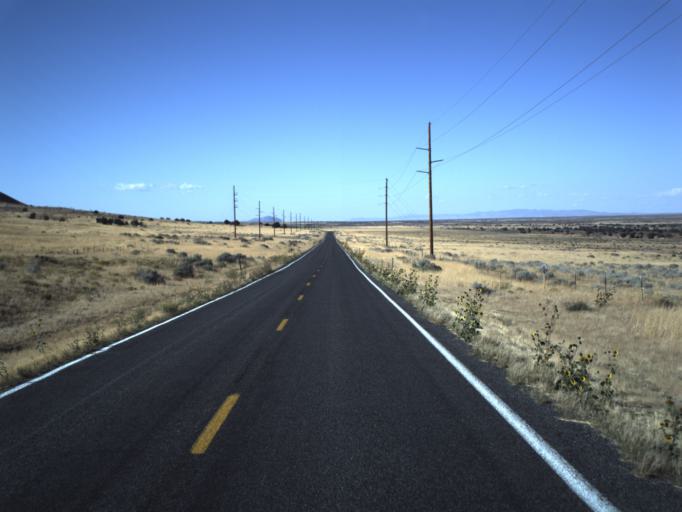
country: US
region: Utah
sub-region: Millard County
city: Delta
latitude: 39.4472
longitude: -112.3099
